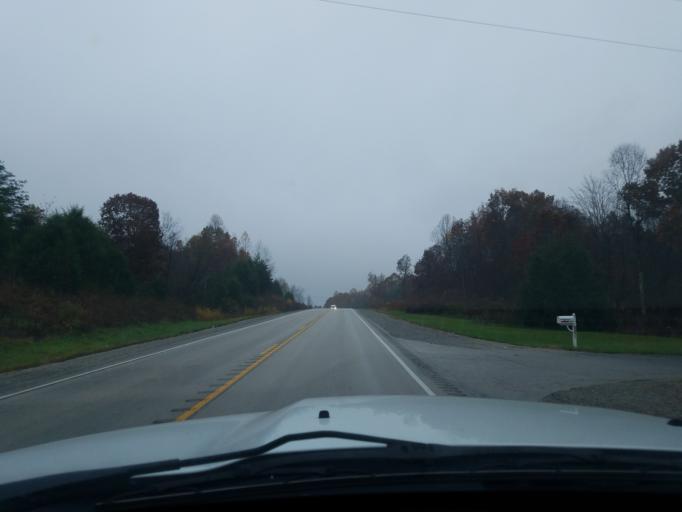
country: US
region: Kentucky
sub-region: Larue County
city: Hodgenville
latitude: 37.4800
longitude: -85.6128
